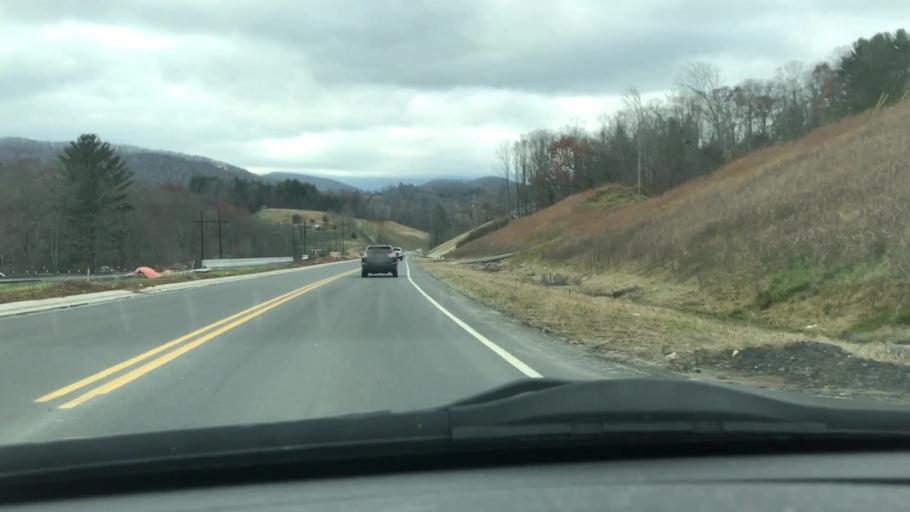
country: US
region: North Carolina
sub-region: Mitchell County
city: Spruce Pine
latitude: 35.9046
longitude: -82.1078
